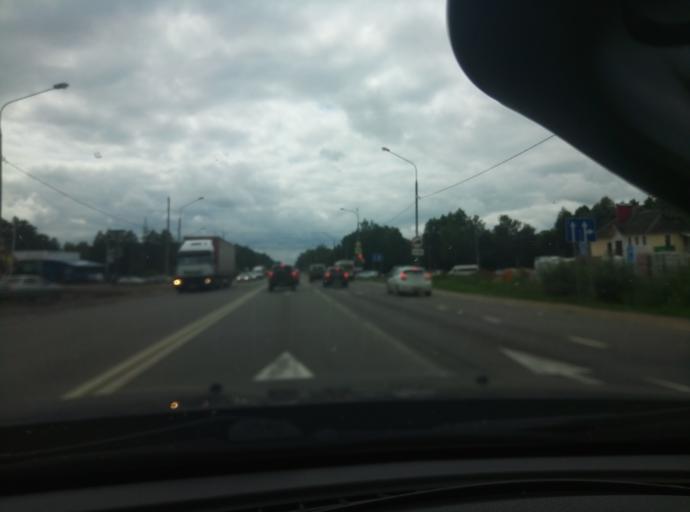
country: RU
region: Kaluga
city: Obninsk
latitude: 55.0897
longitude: 36.6341
